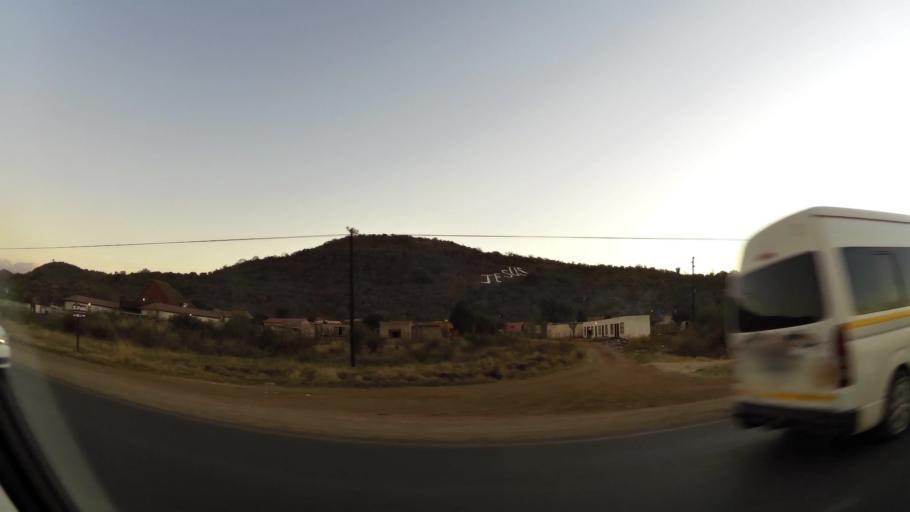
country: ZA
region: Limpopo
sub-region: Waterberg District Municipality
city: Mokopane
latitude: -24.1459
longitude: 28.9709
